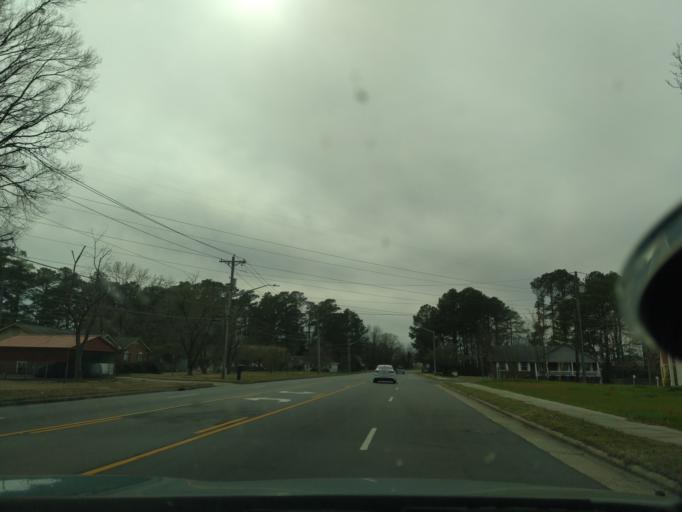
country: US
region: North Carolina
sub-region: Edgecombe County
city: Tarboro
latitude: 35.8963
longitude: -77.5696
